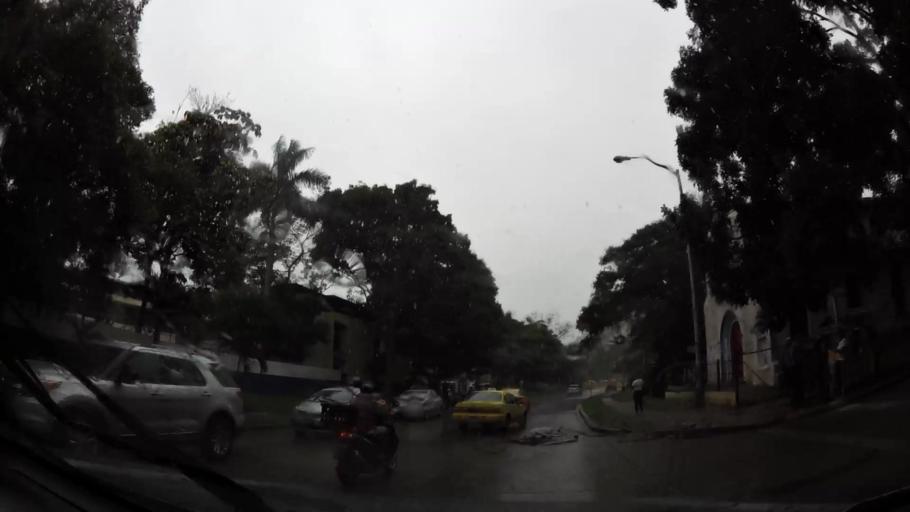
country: PA
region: Panama
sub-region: Distrito de Panama
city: Ancon
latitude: 8.9512
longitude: -79.5546
